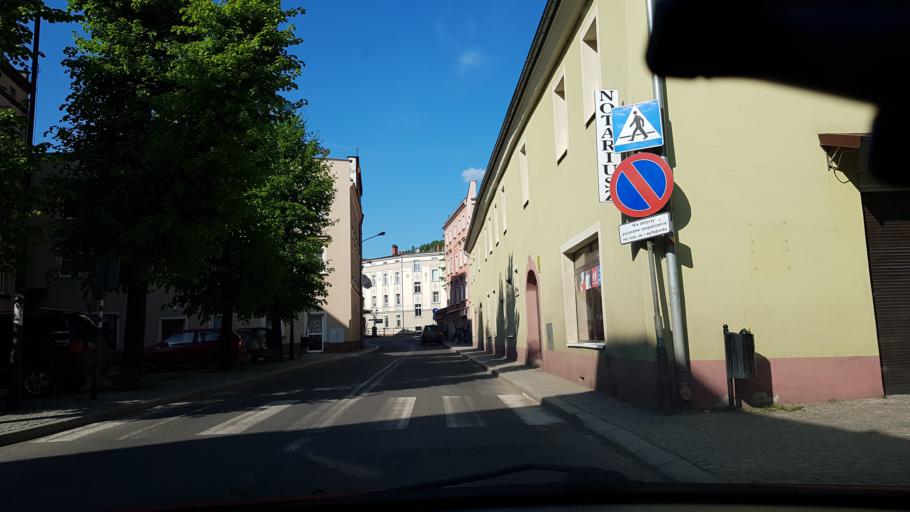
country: PL
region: Lower Silesian Voivodeship
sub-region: Powiat klodzki
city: Nowa Ruda
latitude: 50.5800
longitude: 16.4998
